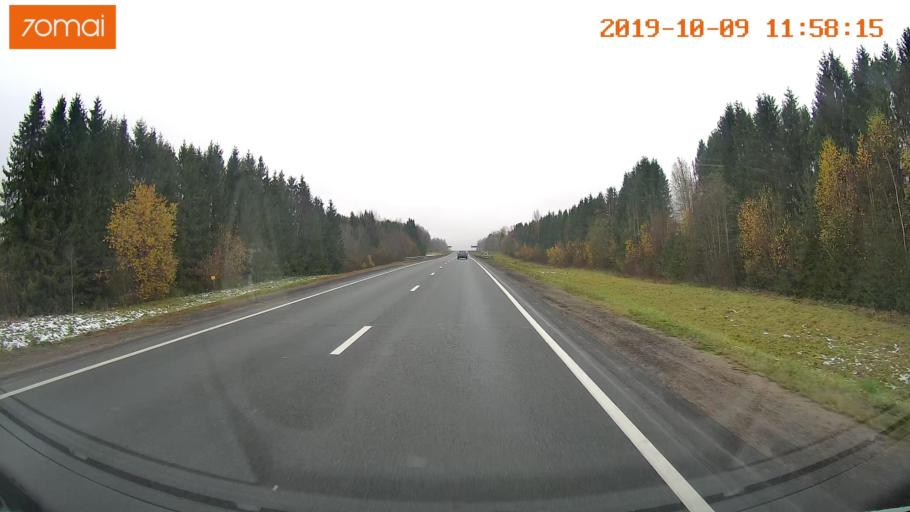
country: RU
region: Vologda
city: Gryazovets
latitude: 58.7207
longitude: 40.2962
